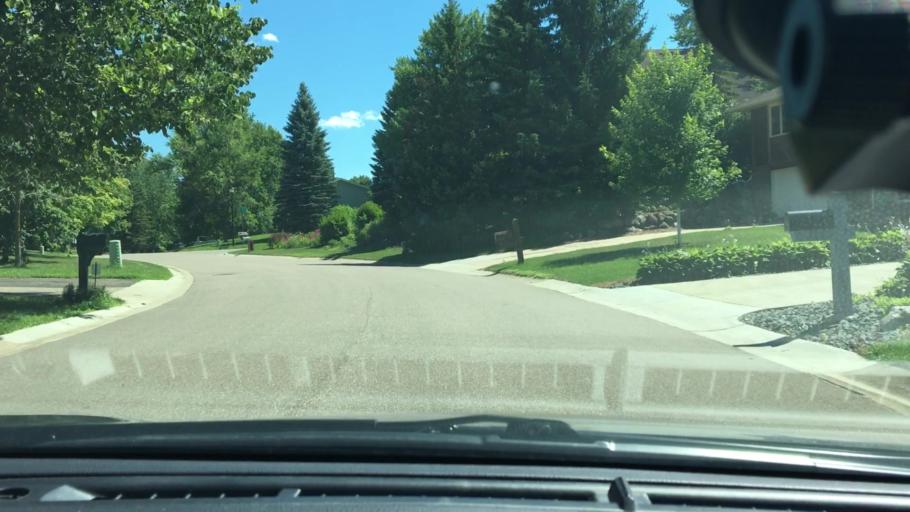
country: US
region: Minnesota
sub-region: Hennepin County
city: Maple Grove
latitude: 45.0685
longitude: -93.4583
